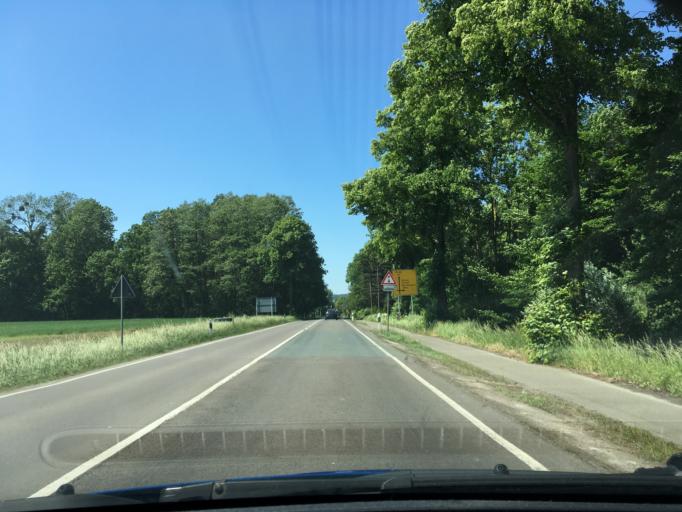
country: DE
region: Lower Saxony
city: Rodenberg
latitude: 52.3269
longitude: 9.3652
